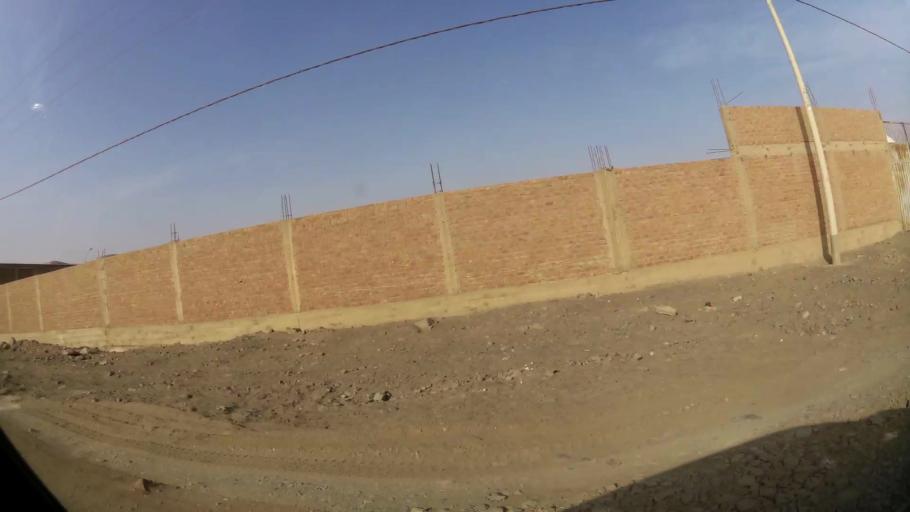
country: PE
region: Lima
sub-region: Lima
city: Santa Rosa
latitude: -11.7529
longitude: -77.1607
